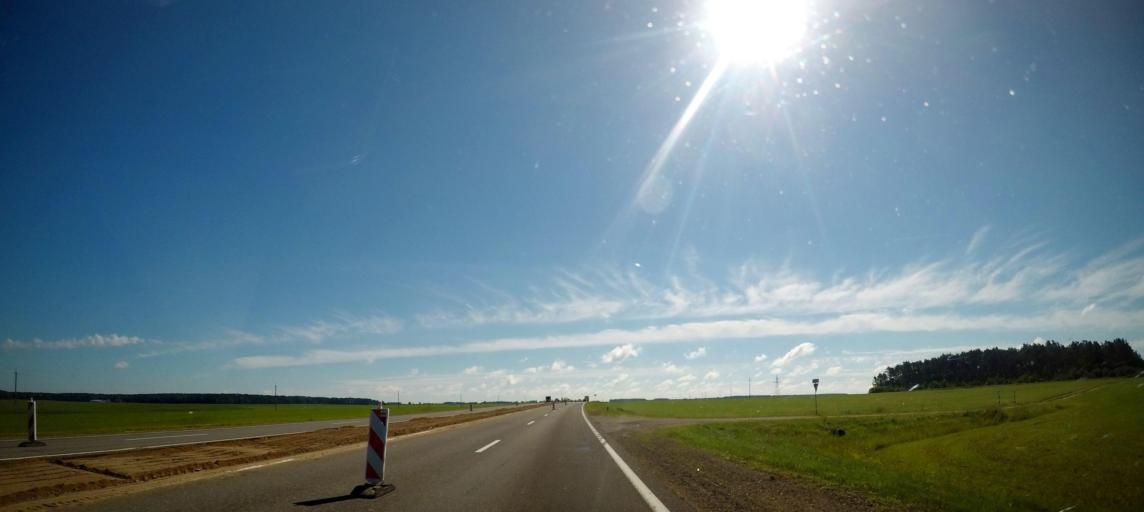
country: BY
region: Grodnenskaya
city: Shchuchin
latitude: 53.6036
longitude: 24.5875
